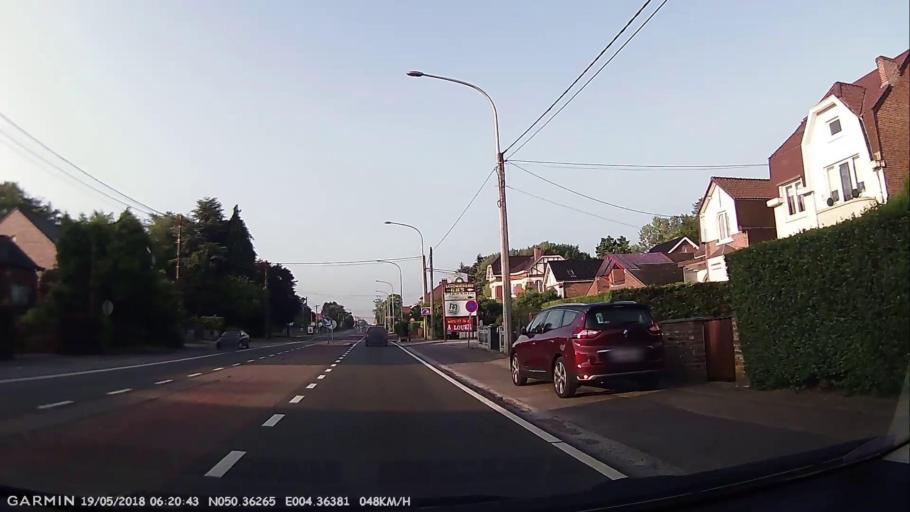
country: BE
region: Wallonia
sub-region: Province du Hainaut
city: Thuin
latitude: 50.3625
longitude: 4.3638
